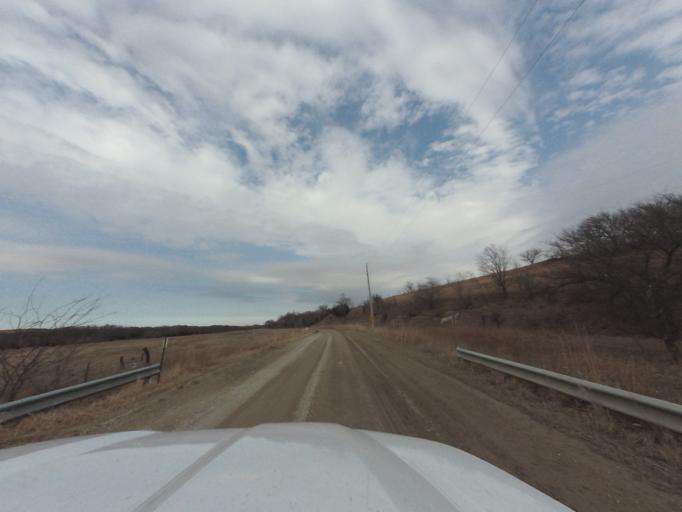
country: US
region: Kansas
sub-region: Chase County
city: Cottonwood Falls
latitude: 38.2654
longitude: -96.7281
